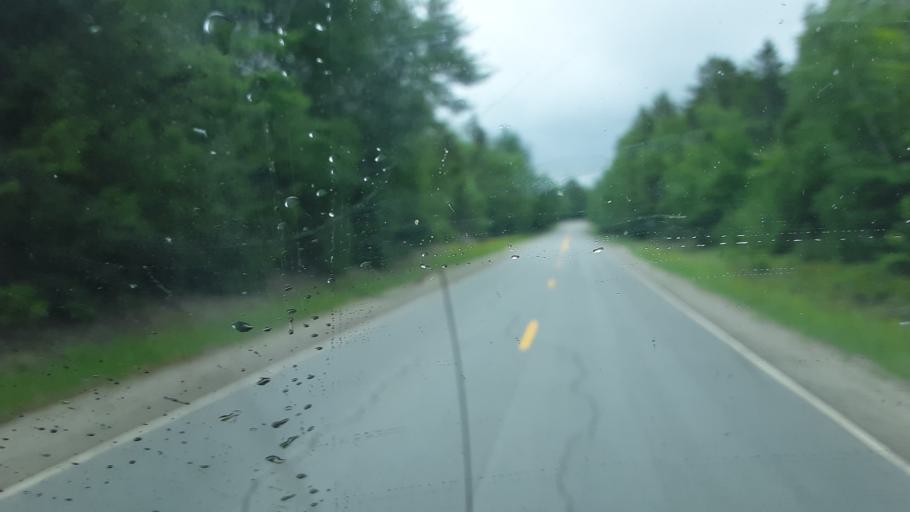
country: US
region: Maine
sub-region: Penobscot County
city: Millinocket
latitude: 45.6878
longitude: -68.7793
